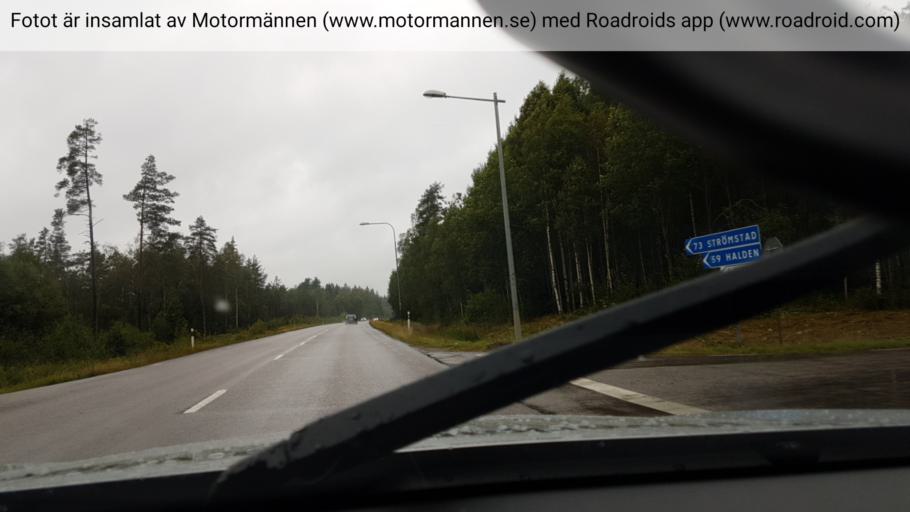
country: SE
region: Vaestra Goetaland
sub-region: Dals-Ed Kommun
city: Ed
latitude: 58.8988
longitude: 11.9614
